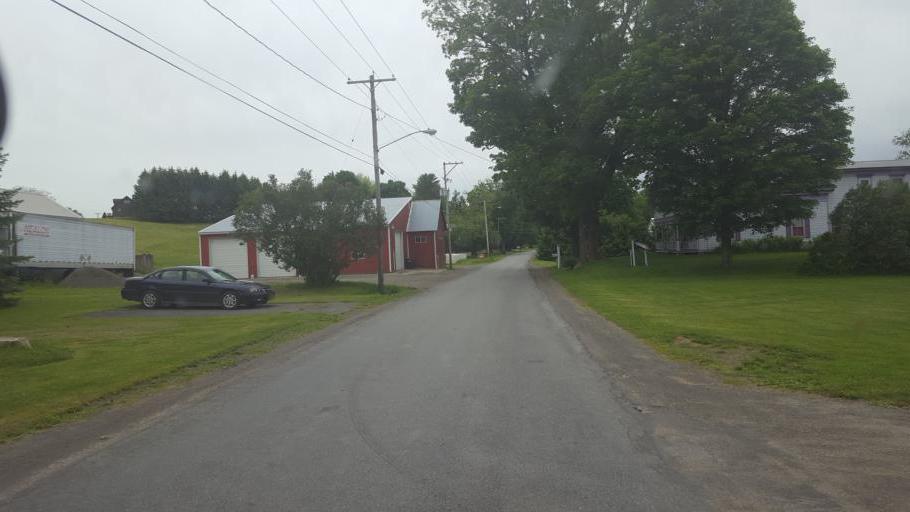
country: US
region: New York
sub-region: Oneida County
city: Waterville
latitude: 42.8447
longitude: -75.2346
